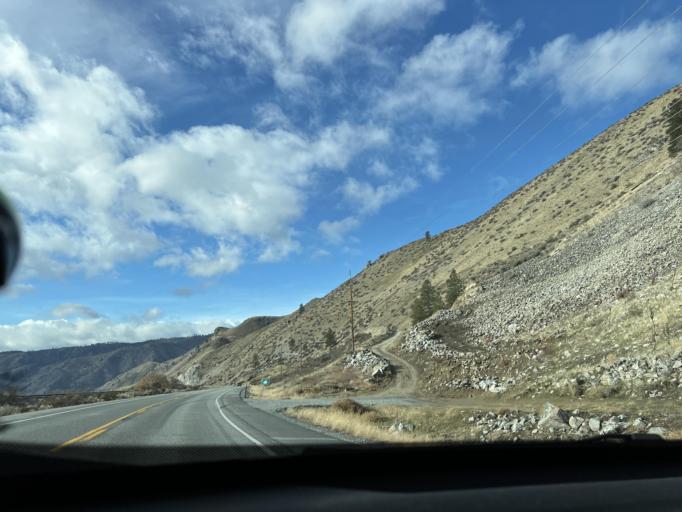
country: US
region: Washington
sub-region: Chelan County
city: Entiat
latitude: 47.7706
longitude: -120.1658
